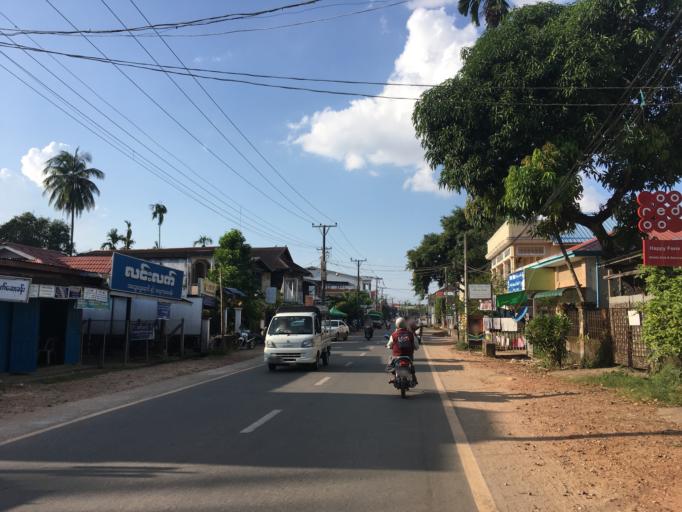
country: MM
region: Mon
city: Mawlamyine
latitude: 16.4598
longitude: 97.6257
